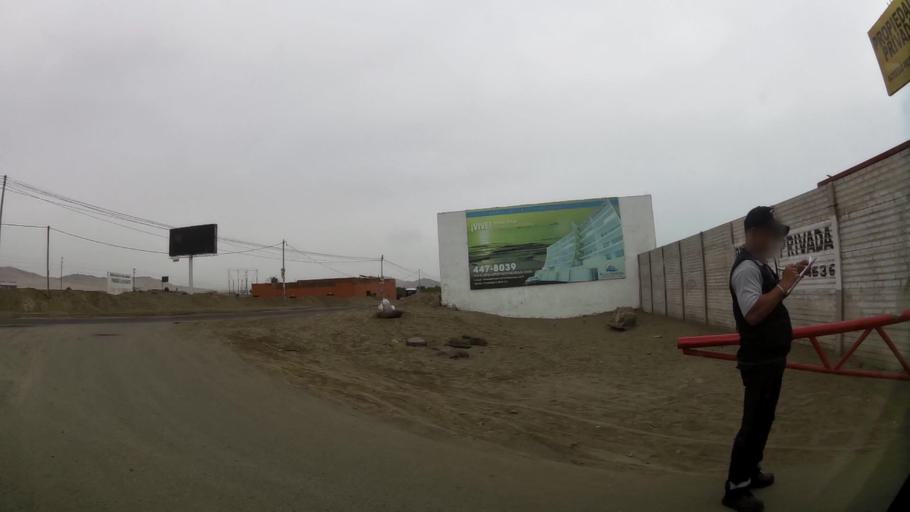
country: PE
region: Lima
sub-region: Lima
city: Punta Hermosa
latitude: -12.3249
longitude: -76.8268
